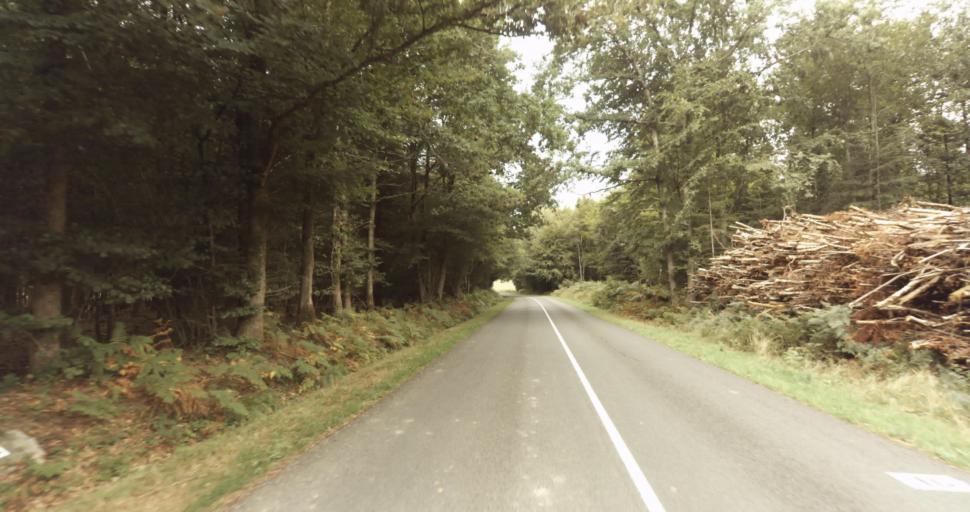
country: FR
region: Lower Normandy
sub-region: Departement de l'Orne
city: Gace
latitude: 48.7972
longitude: 0.3445
